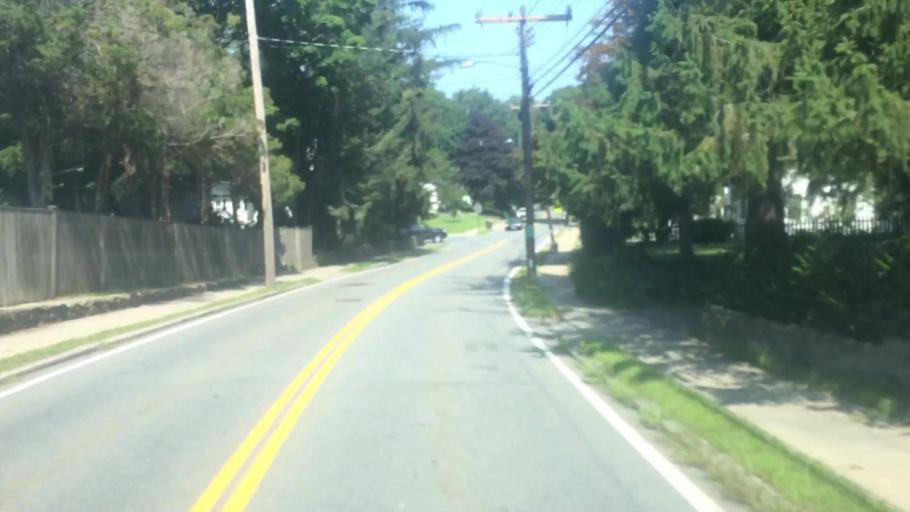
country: US
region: Massachusetts
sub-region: Middlesex County
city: Woburn
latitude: 42.4929
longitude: -71.1497
